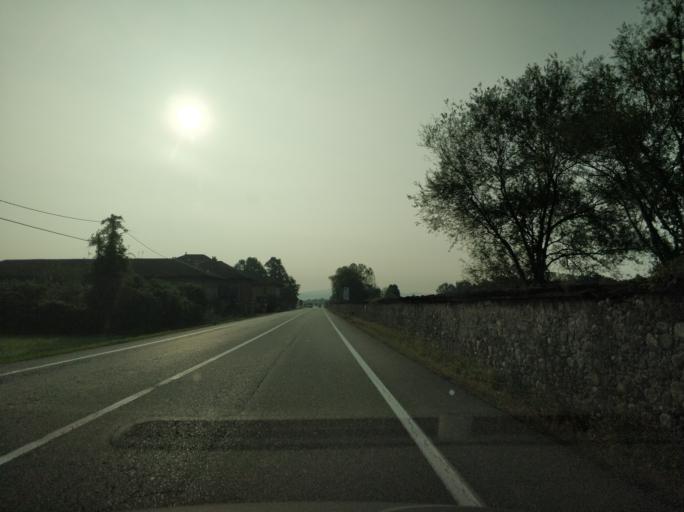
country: IT
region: Piedmont
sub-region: Provincia di Torino
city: Venaria Reale
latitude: 45.1548
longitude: 7.6151
